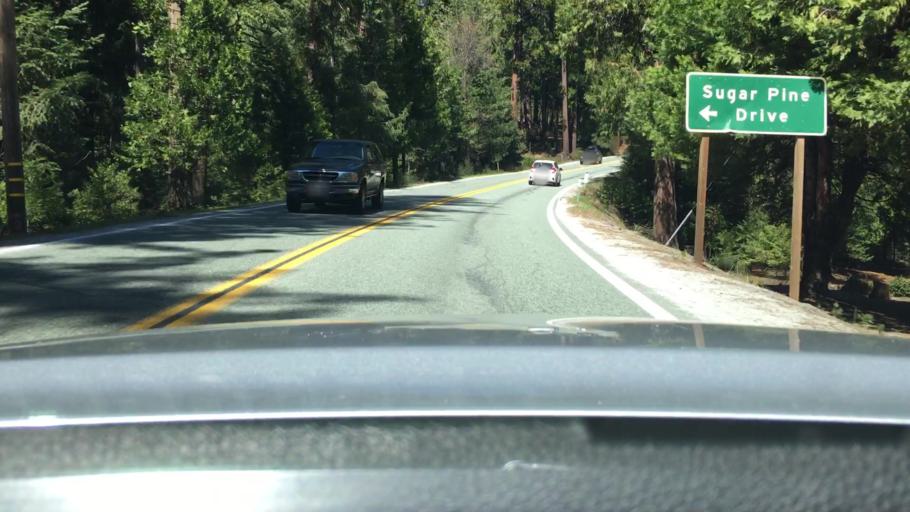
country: US
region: California
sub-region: Amador County
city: Pioneer
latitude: 38.4678
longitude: -120.5277
